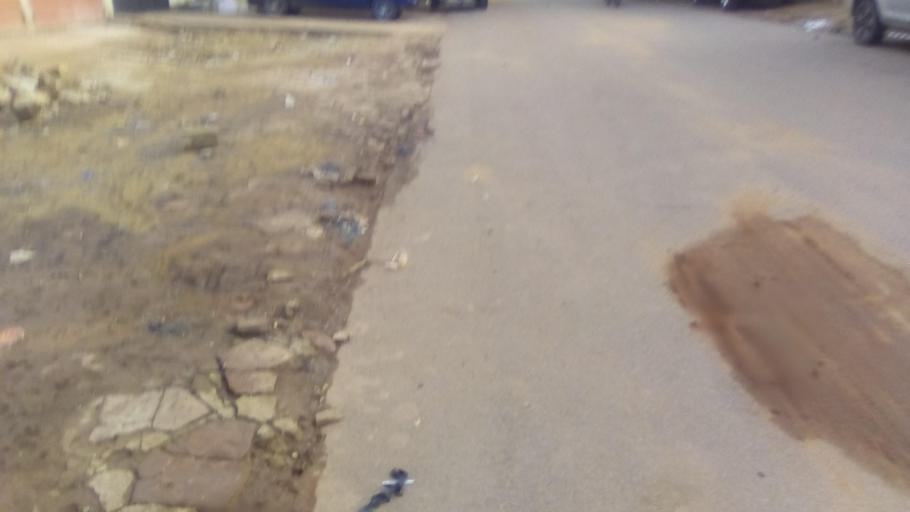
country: ML
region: Bamako
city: Bamako
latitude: 12.6044
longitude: -7.9999
